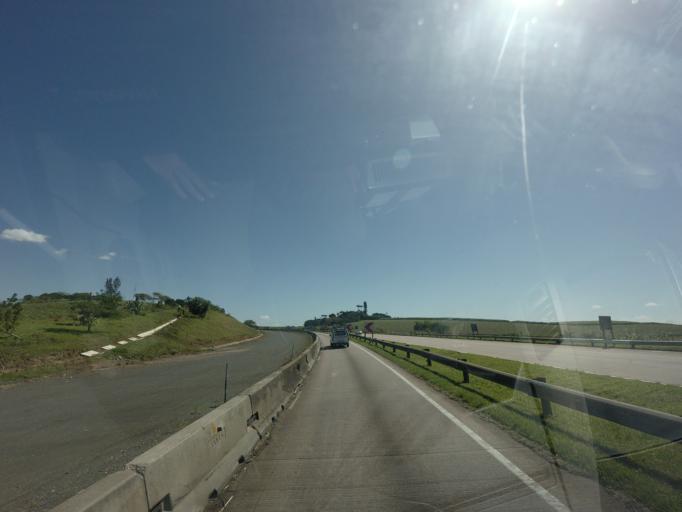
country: ZA
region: KwaZulu-Natal
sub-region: iLembe District Municipality
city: Ballitoville
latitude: -29.4509
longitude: 31.2529
